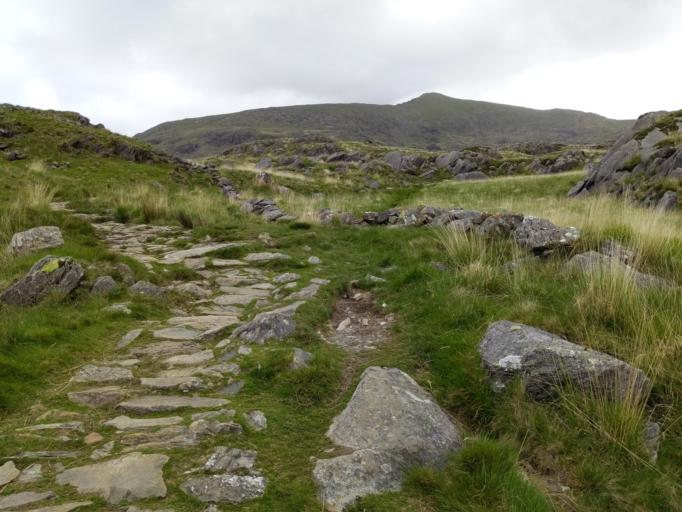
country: GB
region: Wales
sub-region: Gwynedd
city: Llanberis
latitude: 53.0522
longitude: -4.1134
